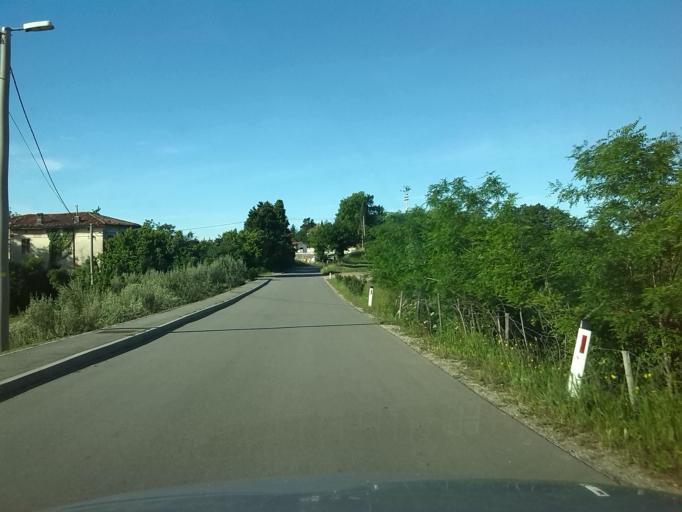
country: SI
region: Brda
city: Dobrovo
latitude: 45.9832
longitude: 13.5207
